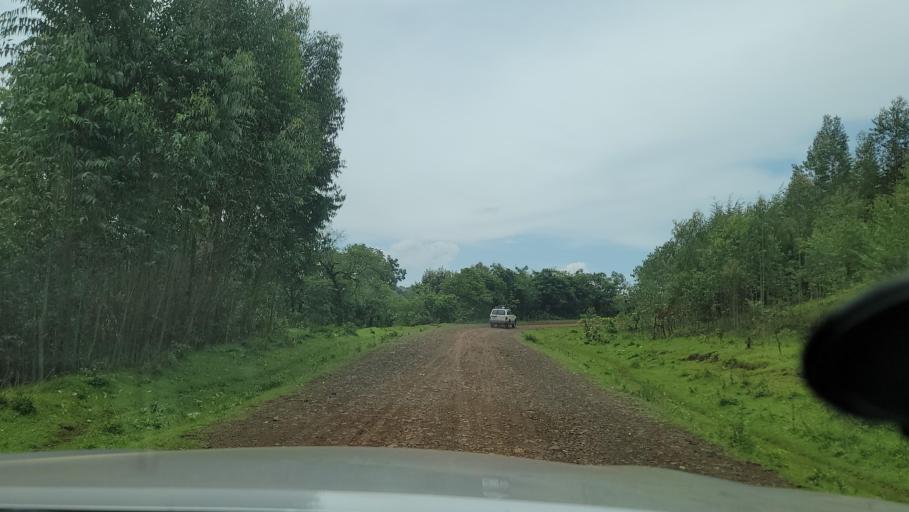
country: ET
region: Oromiya
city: Agaro
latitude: 7.7277
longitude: 36.2565
